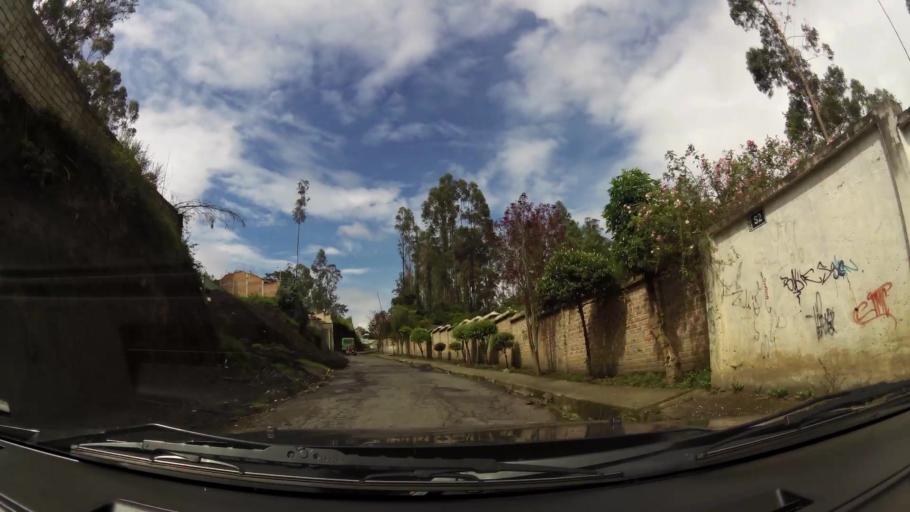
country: EC
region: Pichincha
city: Sangolqui
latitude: -0.3063
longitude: -78.4254
